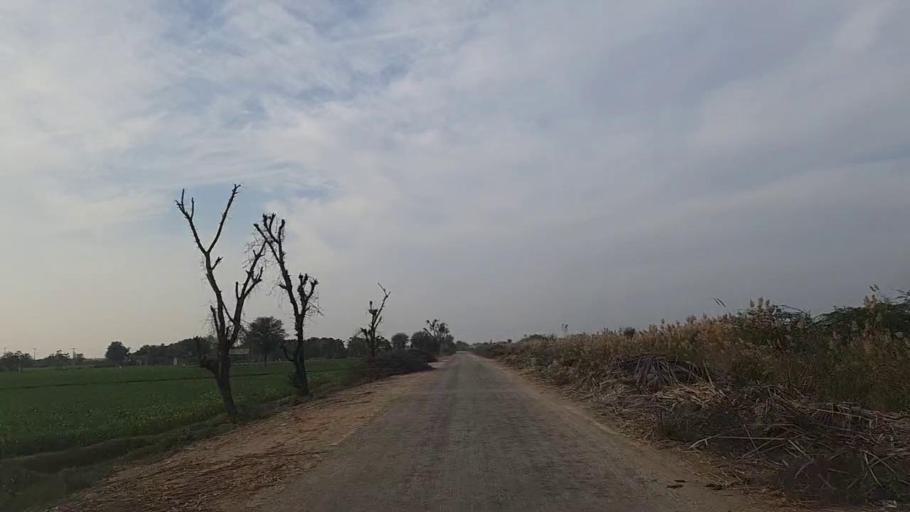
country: PK
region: Sindh
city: Daur
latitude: 26.5006
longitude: 68.4450
